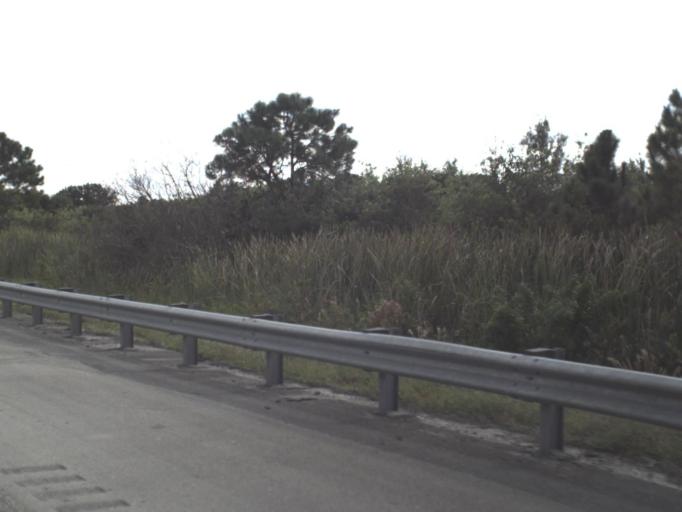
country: US
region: Florida
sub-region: Saint Lucie County
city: Port Saint Lucie
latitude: 27.2810
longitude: -80.3628
